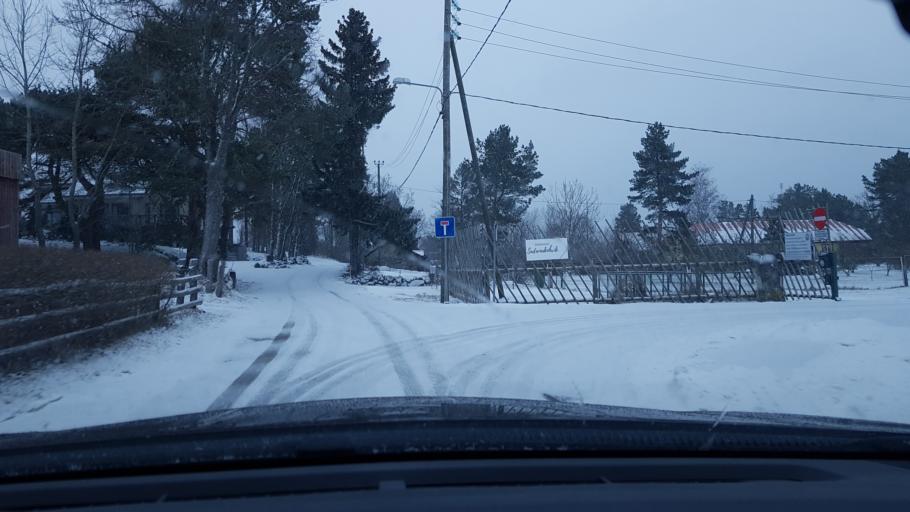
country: EE
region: Harju
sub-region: Raasiku vald
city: Raasiku
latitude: 59.5202
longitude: 25.2750
